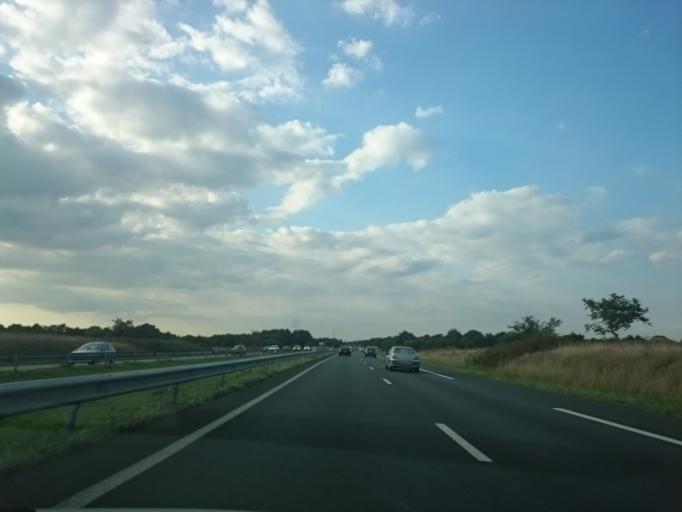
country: FR
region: Pays de la Loire
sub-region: Departement de la Loire-Atlantique
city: Le Temple-de-Bretagne
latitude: 47.3129
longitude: -1.7683
